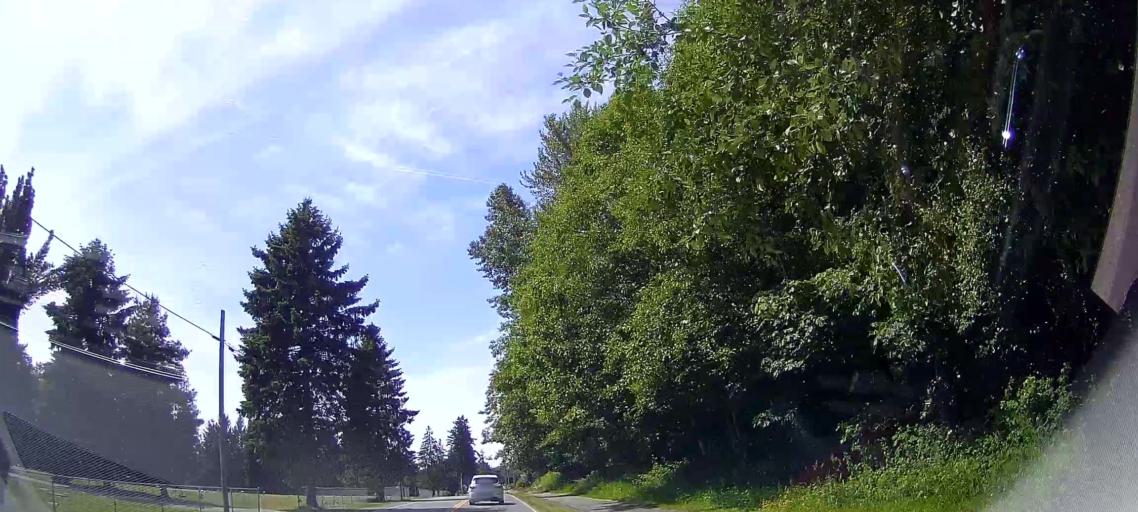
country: US
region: Washington
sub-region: Snohomish County
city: Stanwood
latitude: 48.2334
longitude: -122.3348
